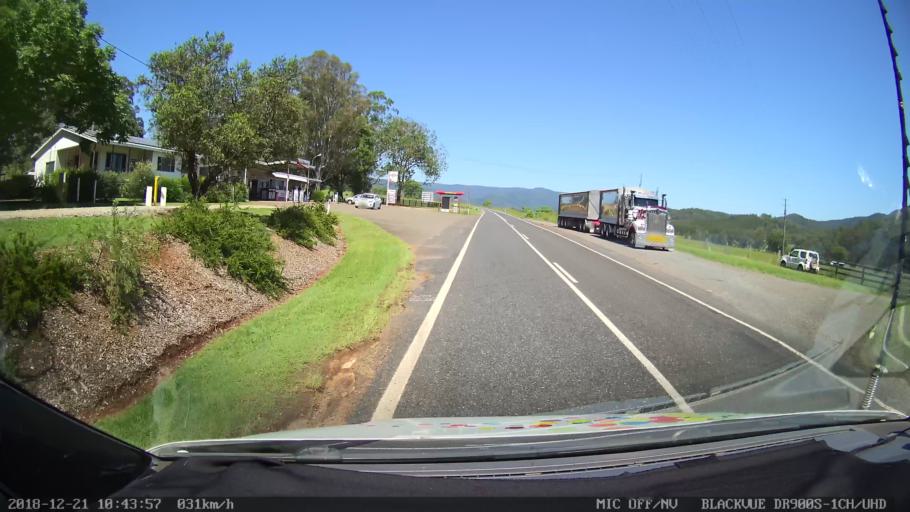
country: AU
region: New South Wales
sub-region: Clarence Valley
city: Gordon
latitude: -29.5767
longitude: 152.5516
